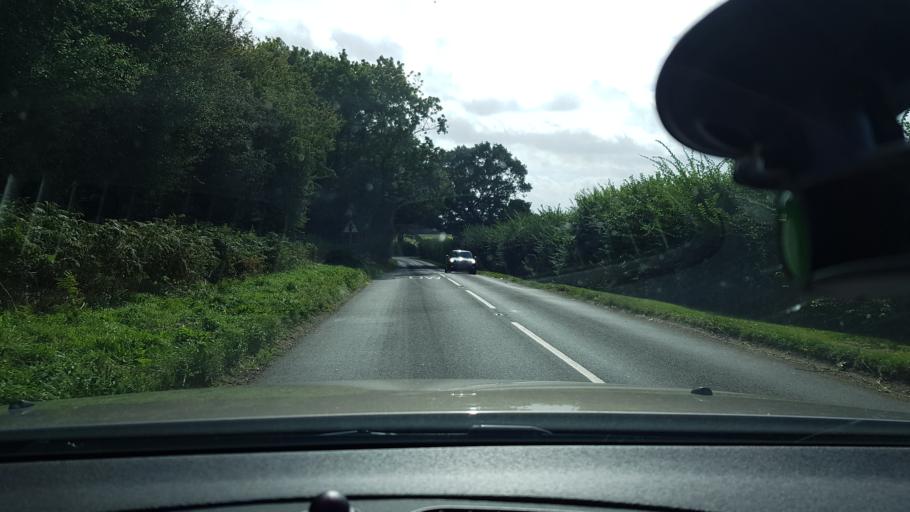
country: GB
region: England
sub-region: West Berkshire
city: Lambourn
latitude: 51.4901
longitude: -1.5491
